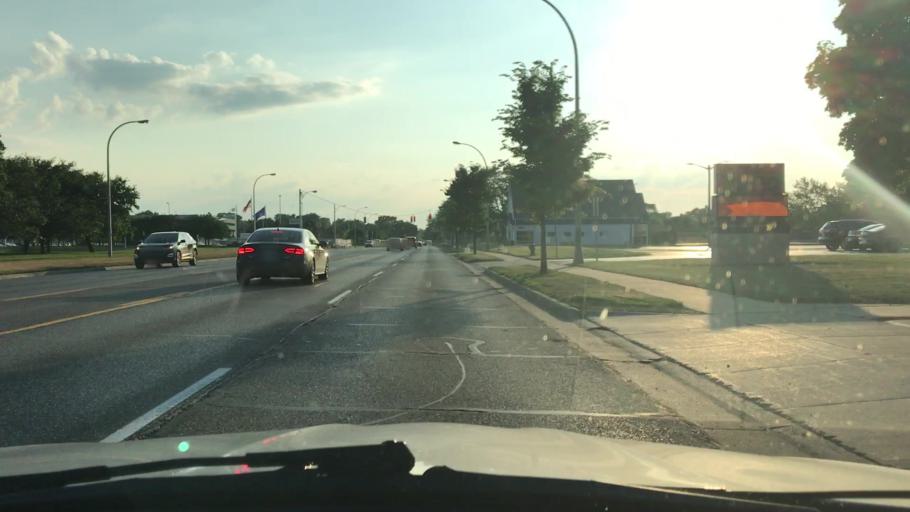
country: US
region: Michigan
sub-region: Oakland County
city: Berkley
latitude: 42.5179
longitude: -83.1901
